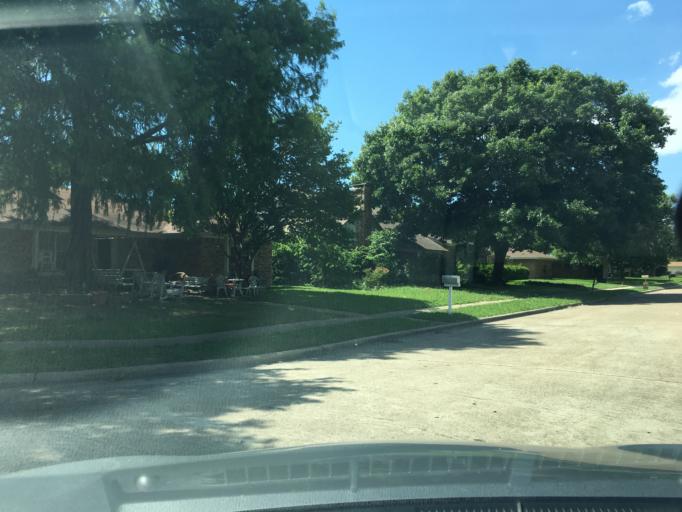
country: US
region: Texas
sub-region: Dallas County
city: Richardson
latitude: 32.9511
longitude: -96.7102
